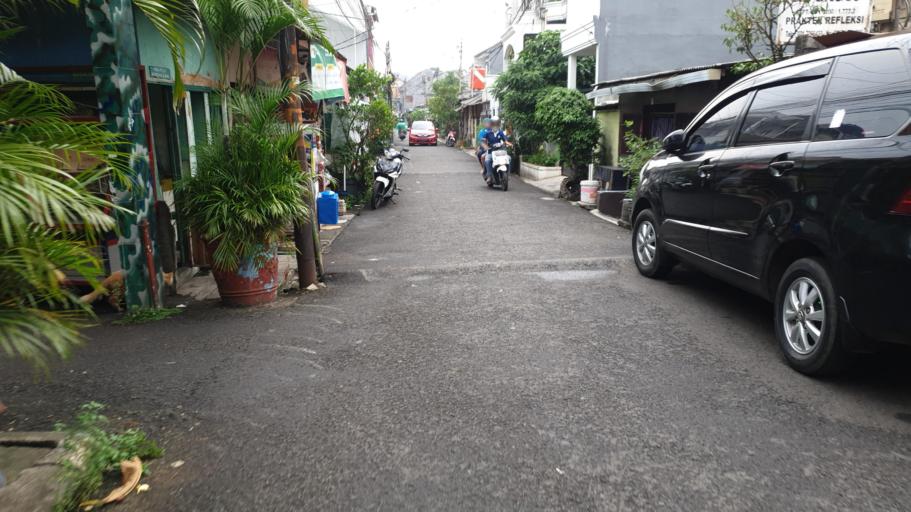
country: ID
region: Jakarta Raya
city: Jakarta
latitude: -6.2586
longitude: 106.7867
